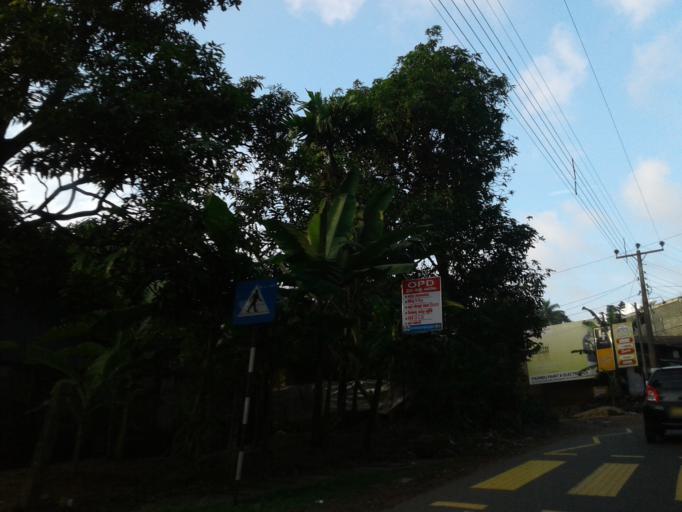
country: LK
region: Western
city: Mulleriyawa
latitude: 6.9702
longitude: 80.0020
